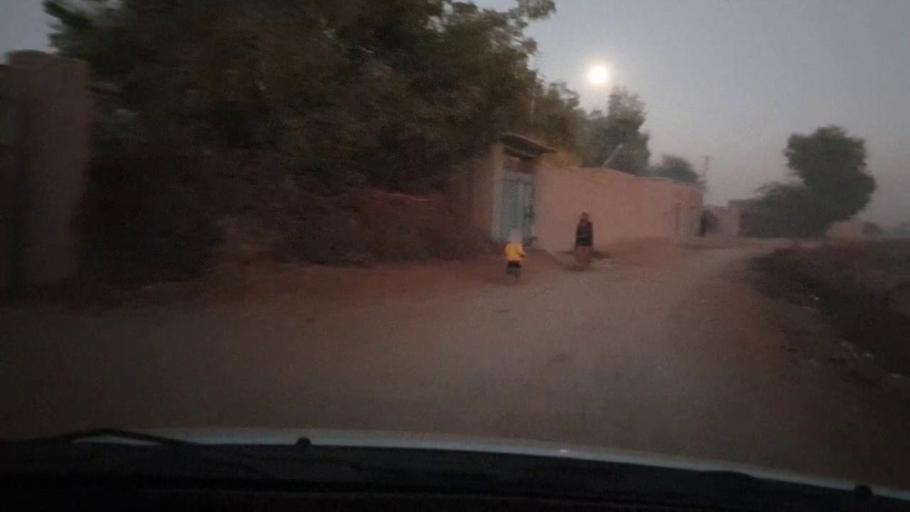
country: PK
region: Sindh
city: Khairpur Nathan Shah
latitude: 27.1342
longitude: 67.7318
